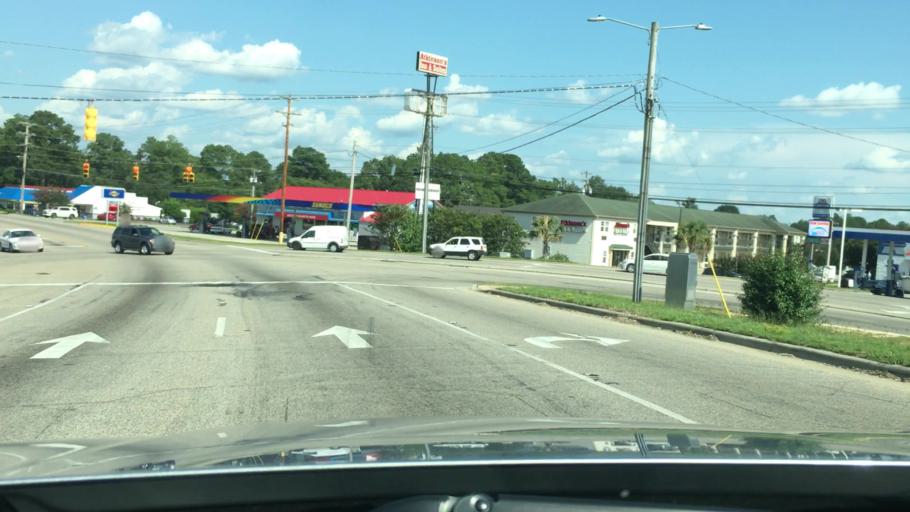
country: US
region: North Carolina
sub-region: Robeson County
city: Lumberton
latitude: 34.6221
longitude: -79.0505
